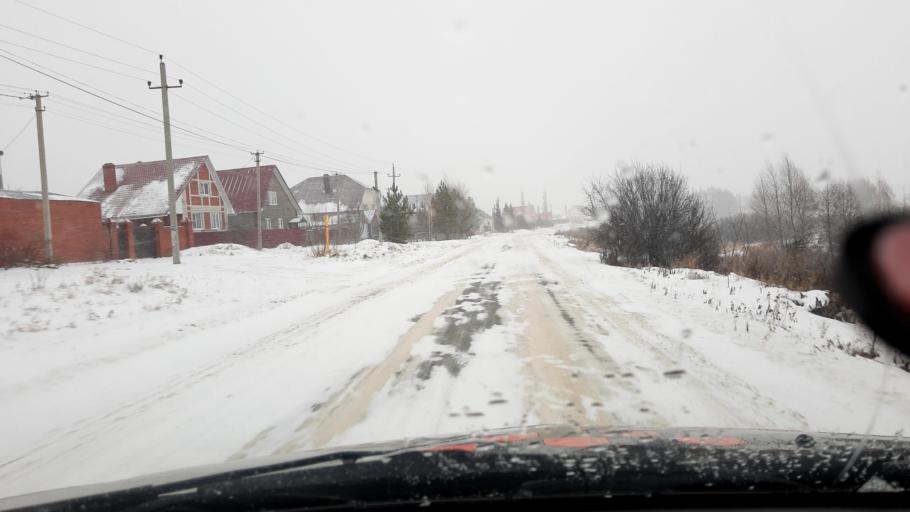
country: RU
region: Bashkortostan
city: Ufa
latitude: 54.5456
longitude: 55.9431
